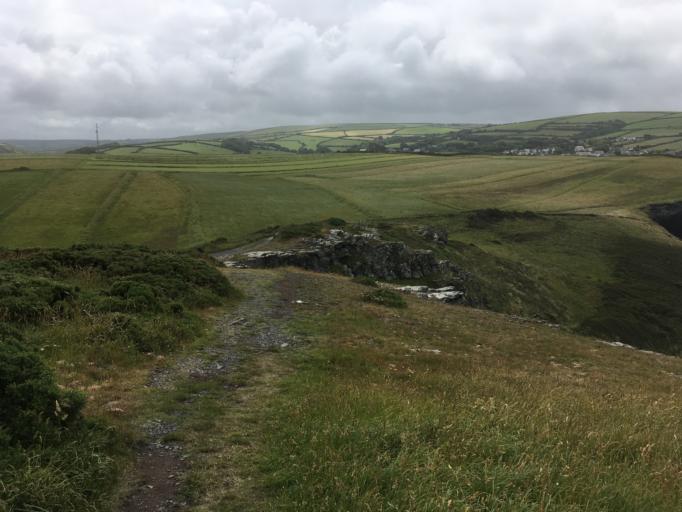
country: GB
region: England
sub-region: Cornwall
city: Tintagel
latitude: 50.6893
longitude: -4.7040
